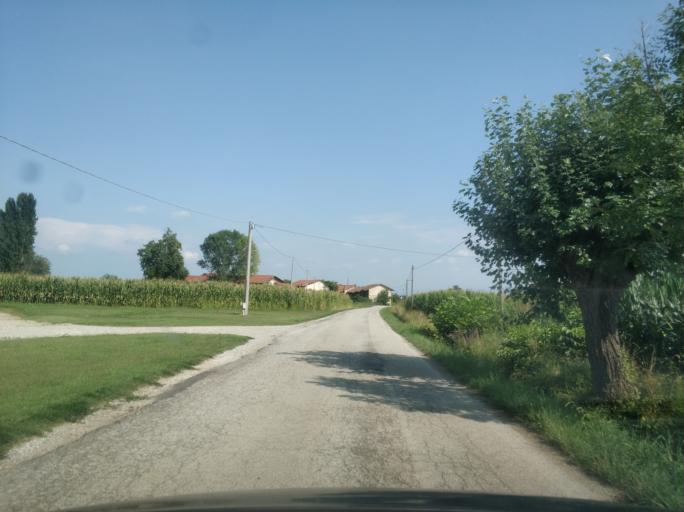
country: IT
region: Piedmont
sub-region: Provincia di Cuneo
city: Roata Rossi
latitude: 44.4536
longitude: 7.4790
